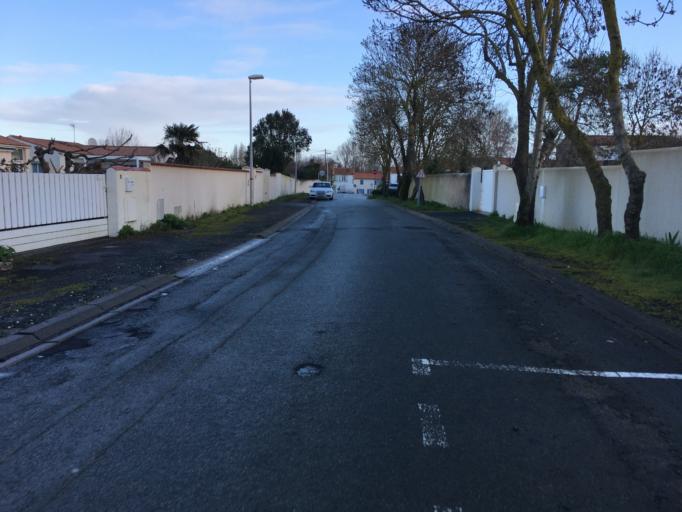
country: FR
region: Poitou-Charentes
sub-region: Departement de la Charente-Maritime
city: Nieul-sur-Mer
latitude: 46.2046
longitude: -1.1652
